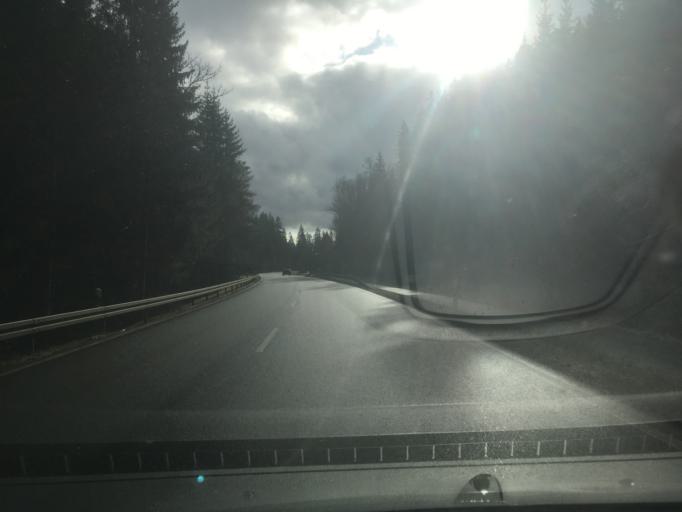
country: DE
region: Baden-Wuerttemberg
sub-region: Freiburg Region
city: Schluchsee
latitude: 47.7840
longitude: 8.1810
